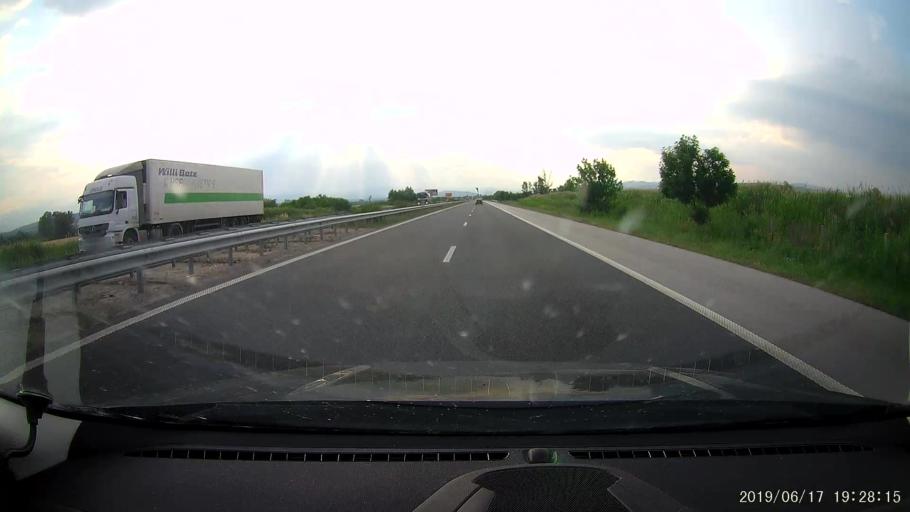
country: BG
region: Pazardzhik
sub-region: Obshtina Pazardzhik
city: Pazardzhik
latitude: 42.2748
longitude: 24.2851
